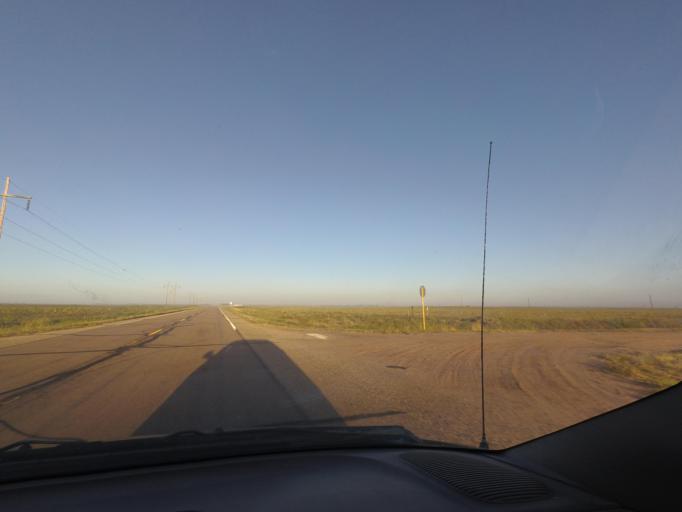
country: US
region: Colorado
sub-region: Yuma County
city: Yuma
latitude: 39.6559
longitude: -102.7256
